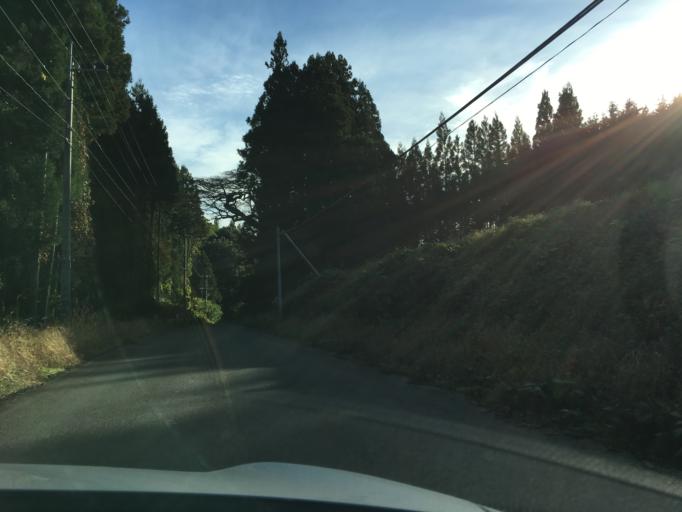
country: JP
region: Fukushima
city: Ishikawa
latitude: 37.2332
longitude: 140.6113
